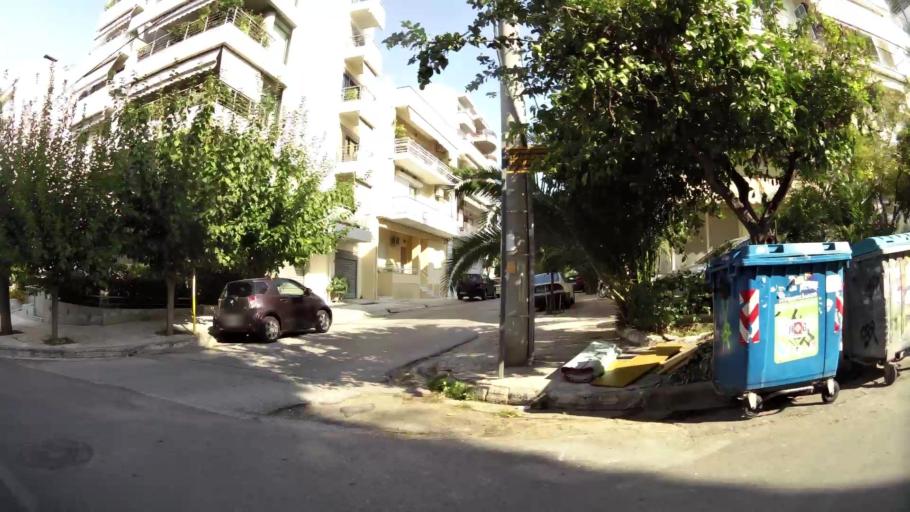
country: GR
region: Attica
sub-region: Nomarchia Athinas
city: Nea Smyrni
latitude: 37.9402
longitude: 23.7093
